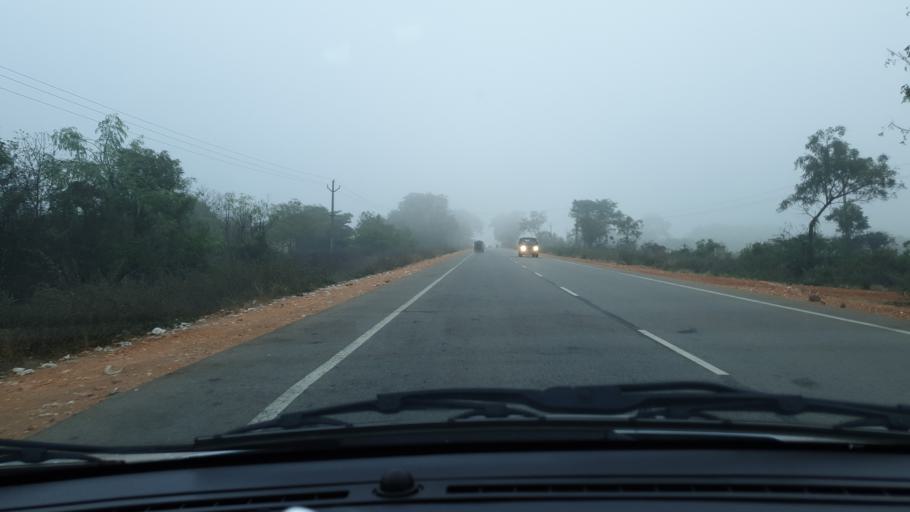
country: IN
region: Telangana
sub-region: Mahbubnagar
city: Nagar Karnul
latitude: 16.6345
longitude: 78.6032
